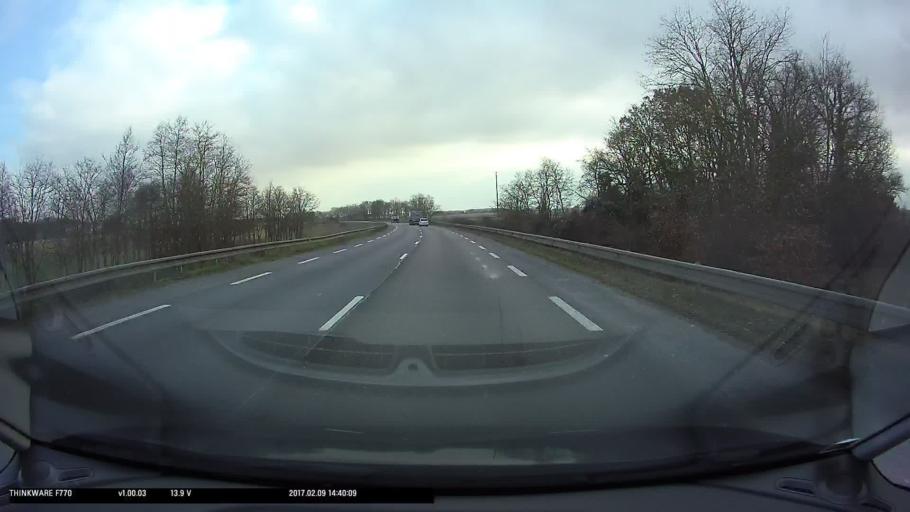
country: FR
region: Centre
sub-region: Departement du Cher
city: Trouy
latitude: 47.0419
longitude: 2.3502
